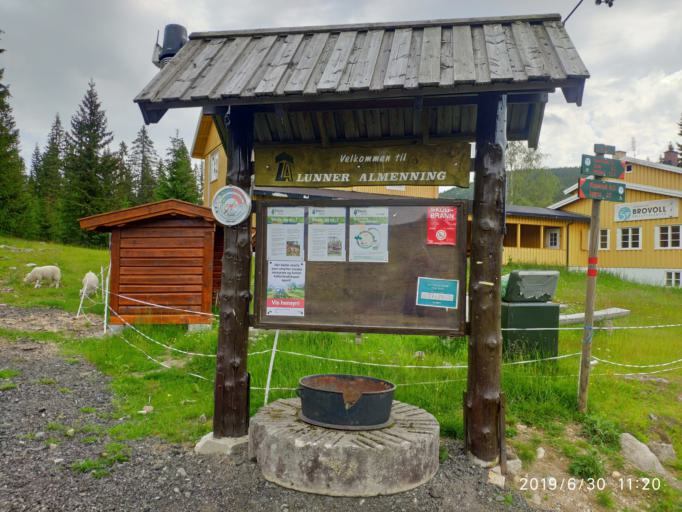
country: NO
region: Oppland
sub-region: Lunner
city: Grua
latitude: 60.2733
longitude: 10.7582
